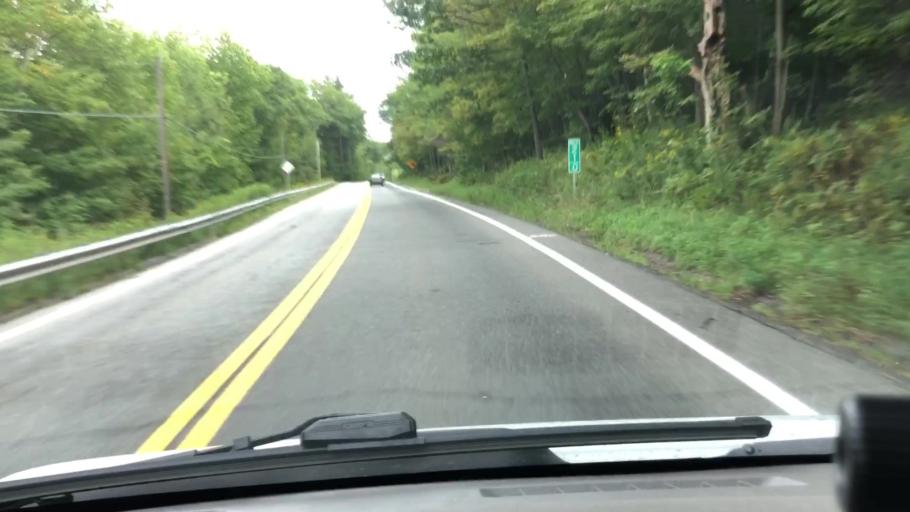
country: US
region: Massachusetts
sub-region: Berkshire County
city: North Adams
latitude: 42.6591
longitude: -73.0057
